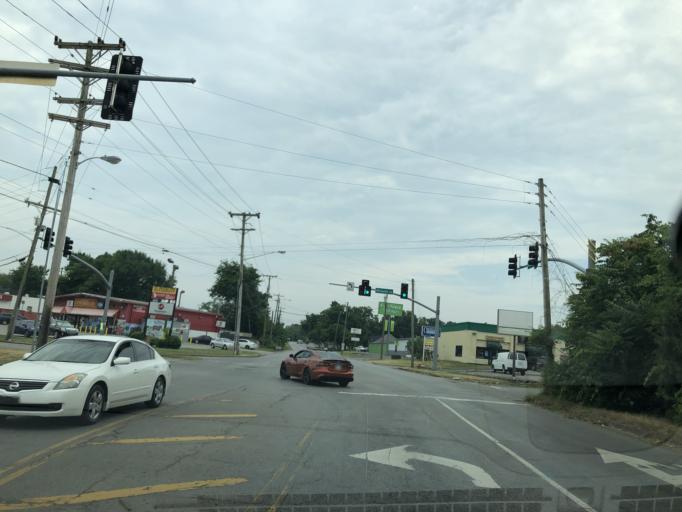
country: US
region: Tennessee
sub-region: Davidson County
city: Oak Hill
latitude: 36.0692
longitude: -86.6840
